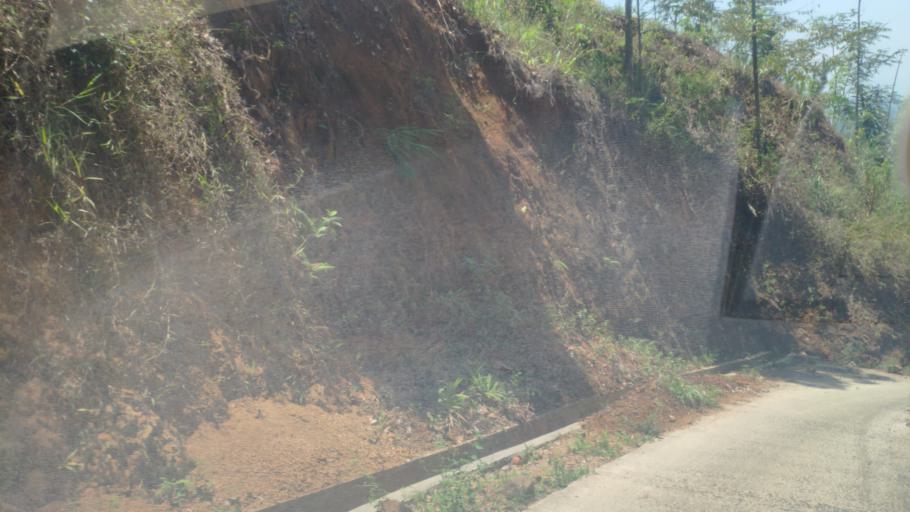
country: ID
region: Central Java
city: Buaran
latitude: -7.2872
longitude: 109.5876
